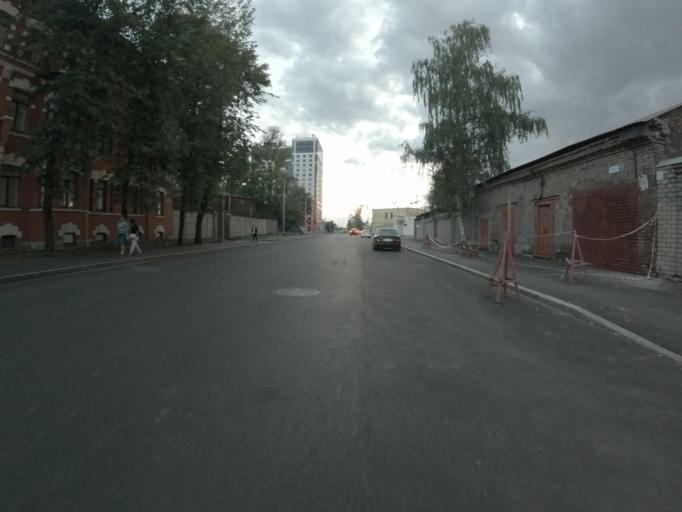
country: RU
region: St.-Petersburg
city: Admiralteisky
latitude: 59.8964
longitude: 30.3157
